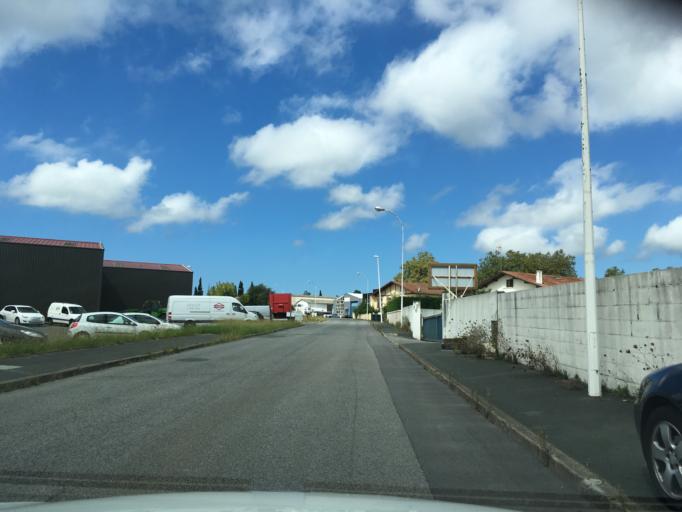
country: FR
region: Aquitaine
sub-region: Departement des Pyrenees-Atlantiques
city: Boucau
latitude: 43.5107
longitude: -1.4311
